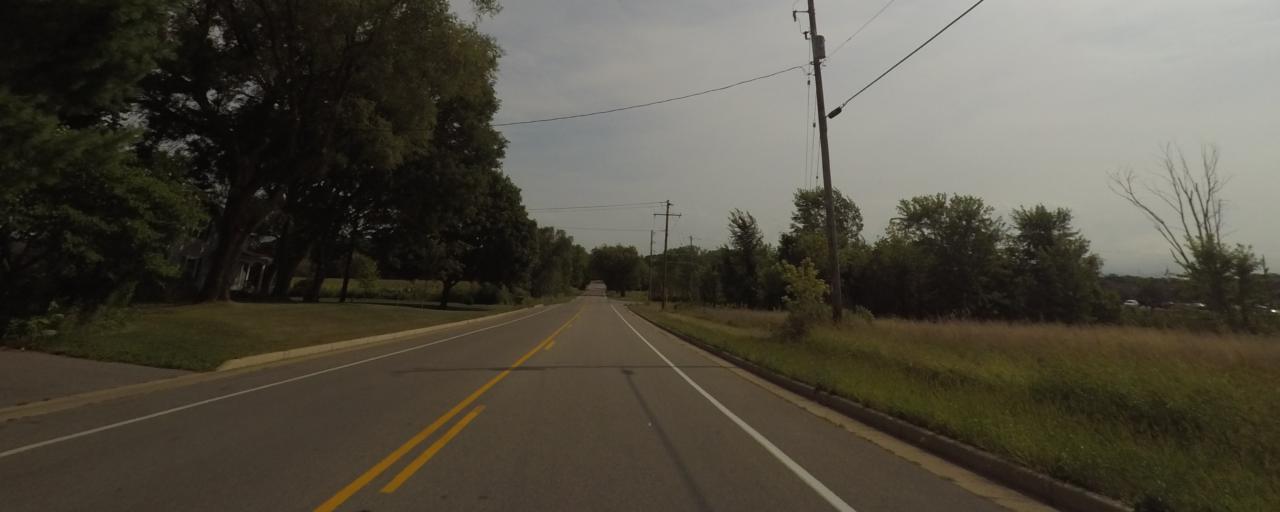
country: US
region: Wisconsin
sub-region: Jefferson County
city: Jefferson
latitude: 42.9948
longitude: -88.8278
